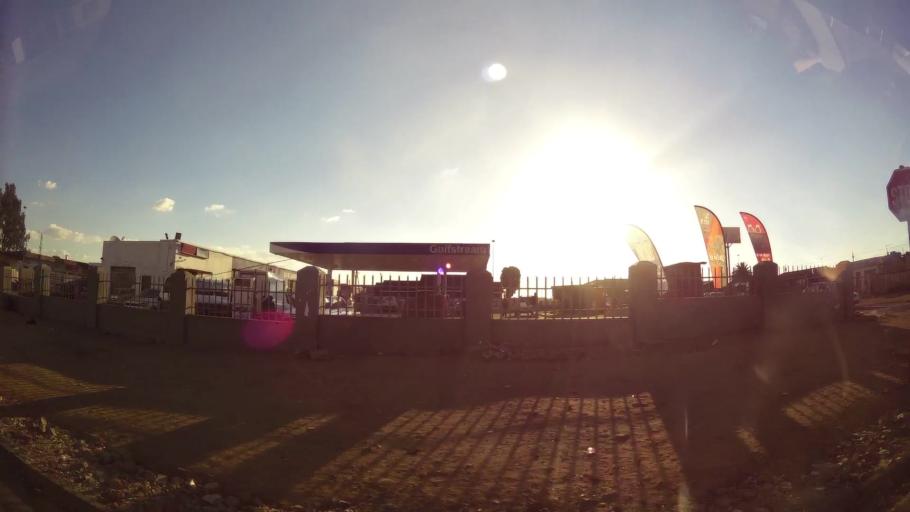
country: ZA
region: Mpumalanga
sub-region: Nkangala District Municipality
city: Witbank
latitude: -25.8726
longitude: 29.1822
